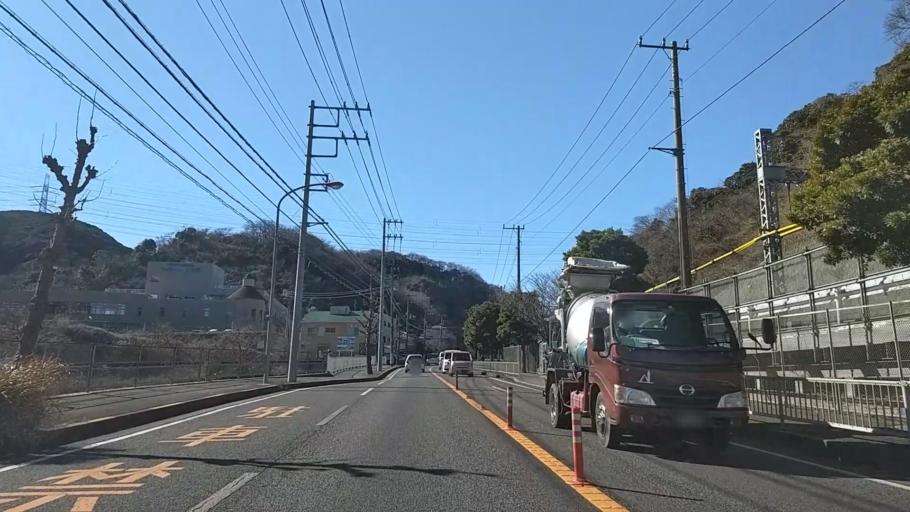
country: JP
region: Kanagawa
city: Yokosuka
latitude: 35.2242
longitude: 139.6986
